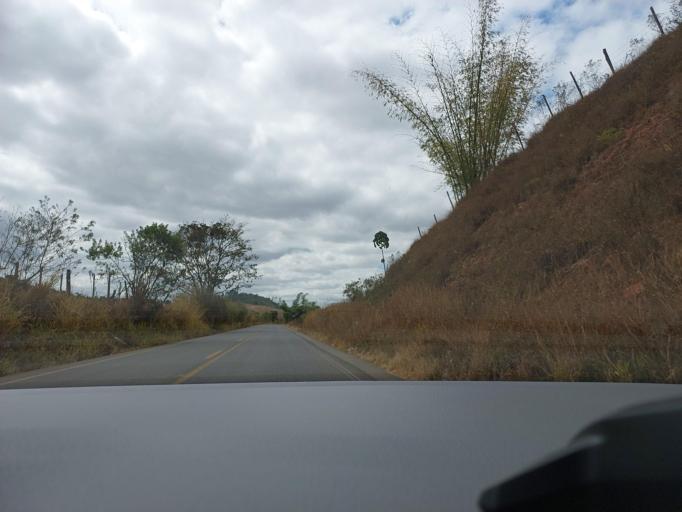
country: BR
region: Minas Gerais
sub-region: Vicosa
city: Vicosa
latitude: -20.8302
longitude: -42.7528
